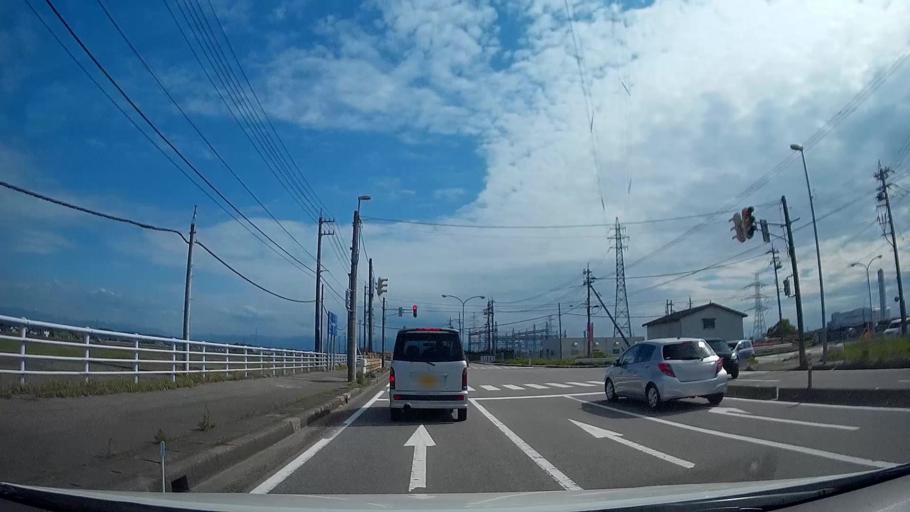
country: JP
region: Toyama
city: Kuragaki-kosugi
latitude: 36.7475
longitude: 137.1294
